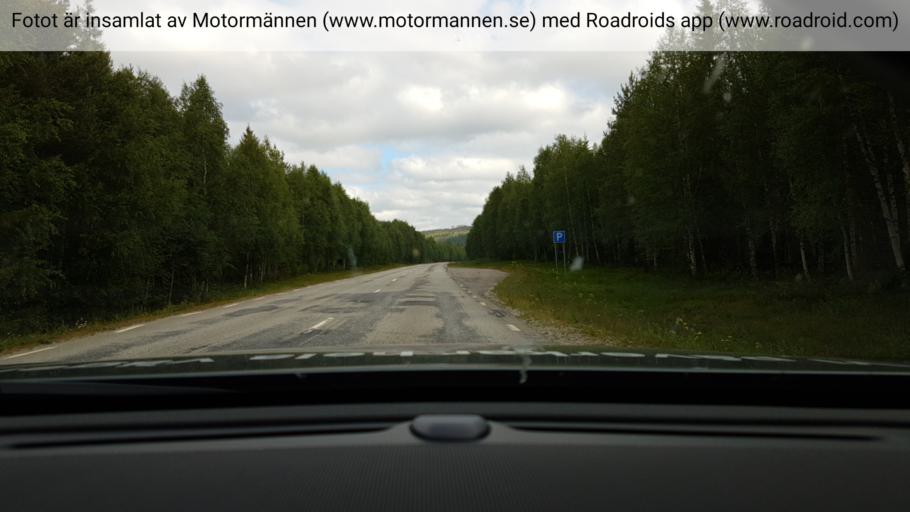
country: SE
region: Vaesterbotten
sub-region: Mala Kommun
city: Mala
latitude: 64.9285
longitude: 18.6183
